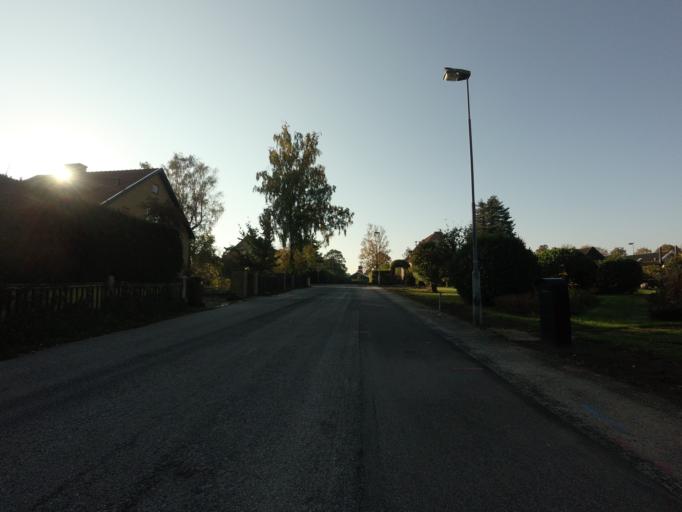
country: SE
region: Skane
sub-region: Staffanstorps Kommun
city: Hjaerup
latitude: 55.6533
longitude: 13.1077
